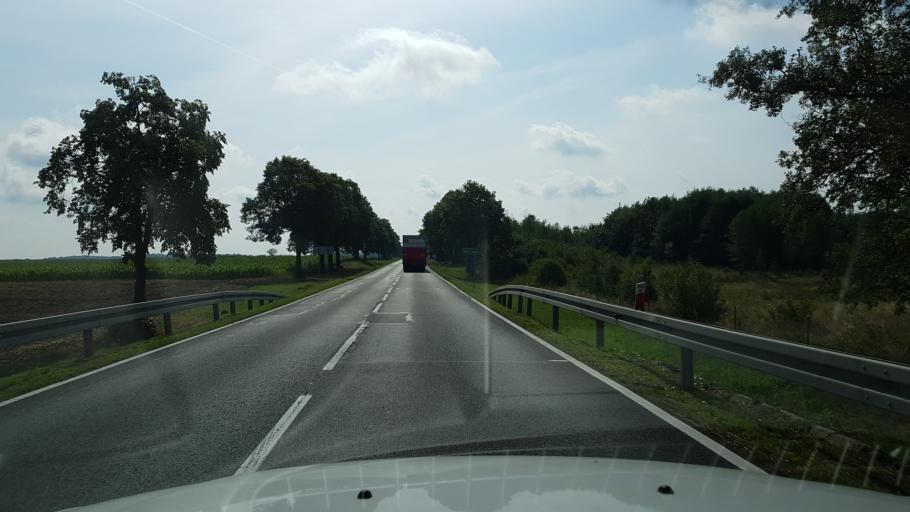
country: PL
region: West Pomeranian Voivodeship
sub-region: Powiat walecki
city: Walcz
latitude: 53.3285
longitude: 16.3023
